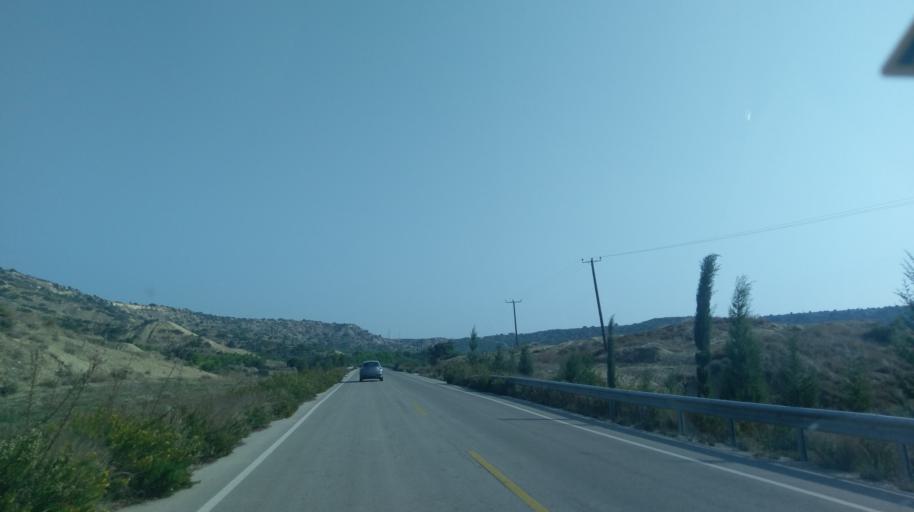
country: CY
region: Ammochostos
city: Leonarisso
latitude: 35.4773
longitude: 34.1220
